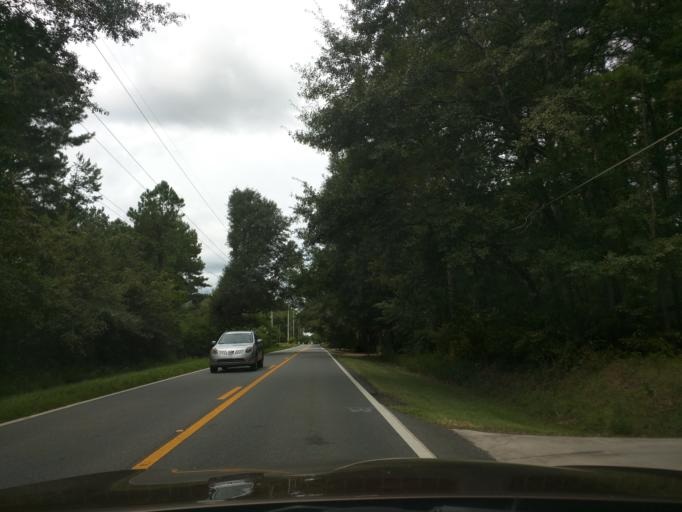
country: US
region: Florida
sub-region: Leon County
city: Tallahassee
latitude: 30.5598
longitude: -84.1899
